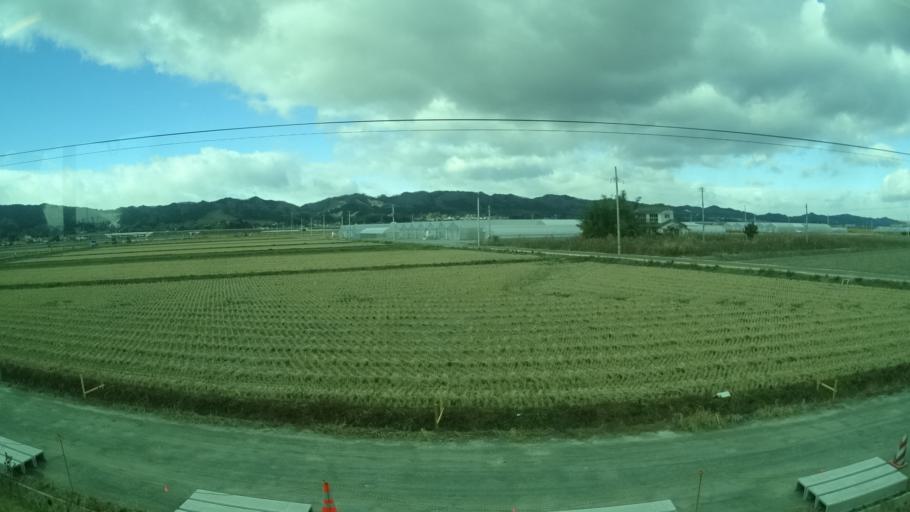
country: JP
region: Miyagi
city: Watari
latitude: 37.9826
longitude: 140.8887
